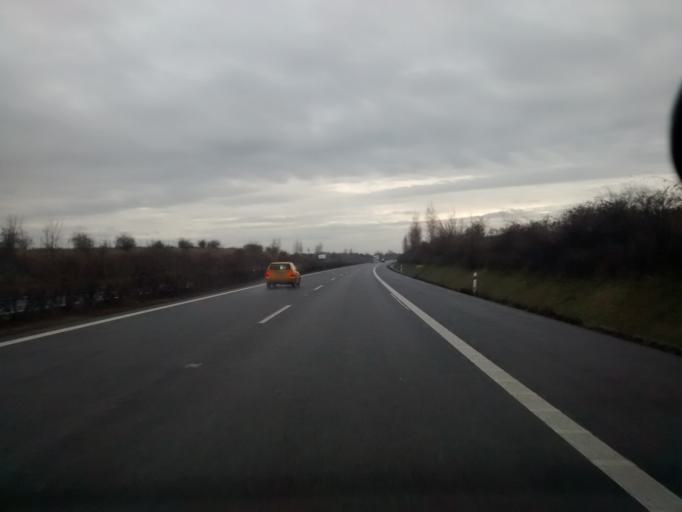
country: CZ
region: Ustecky
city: Roudnice nad Labem
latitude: 50.3544
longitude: 14.2740
